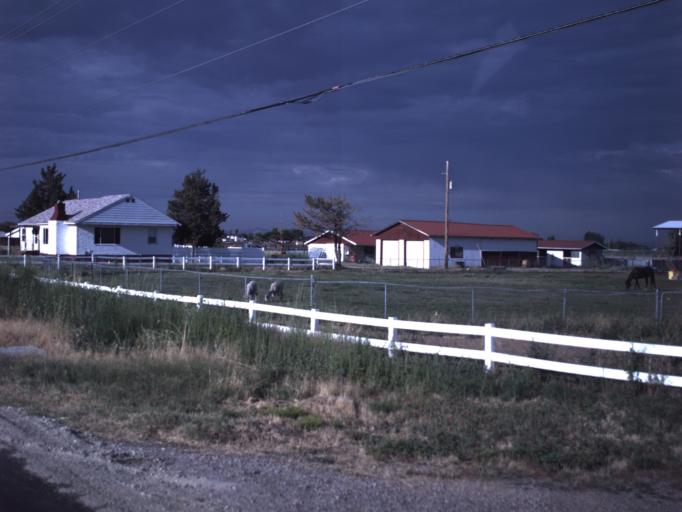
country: US
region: Utah
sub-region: Weber County
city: West Haven
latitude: 41.2164
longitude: -112.0929
